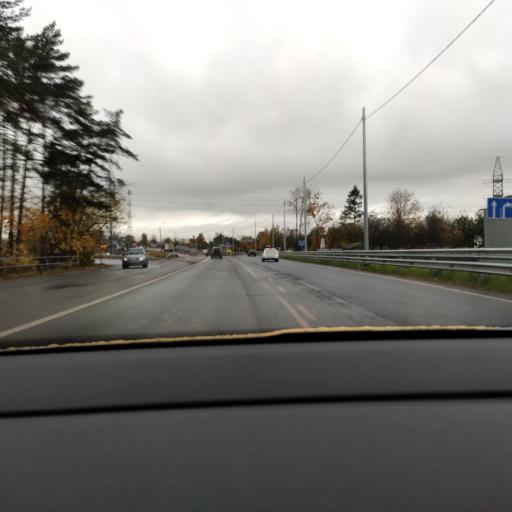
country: RU
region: Moskovskaya
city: Lesnyye Polyany
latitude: 55.9858
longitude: 37.8771
